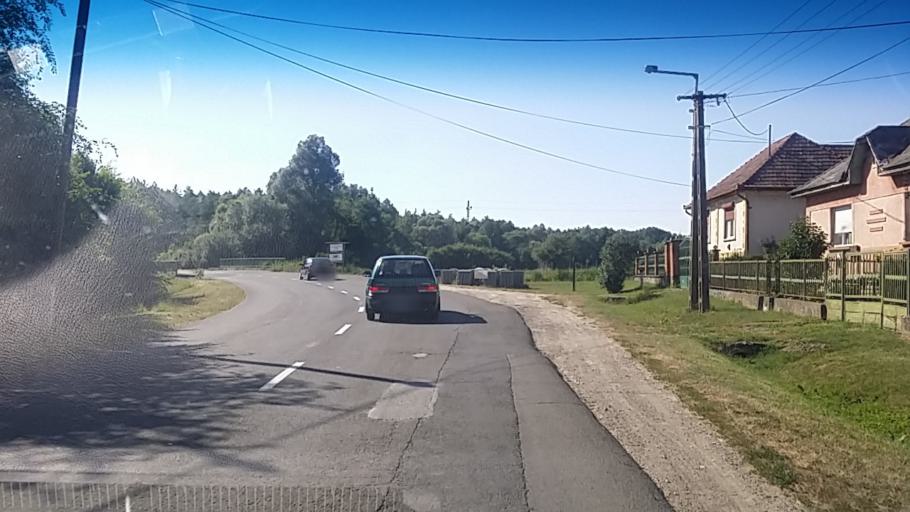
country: HU
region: Nograd
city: Retsag
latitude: 47.9306
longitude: 19.1690
